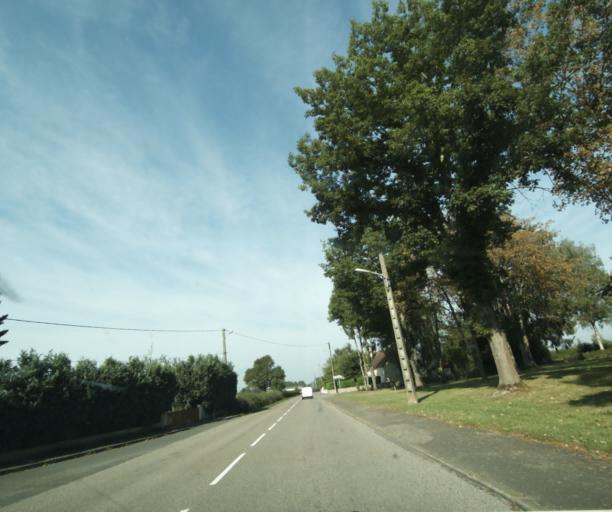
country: FR
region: Bourgogne
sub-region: Departement de Saone-et-Loire
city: Genelard
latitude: 46.5766
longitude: 4.2499
